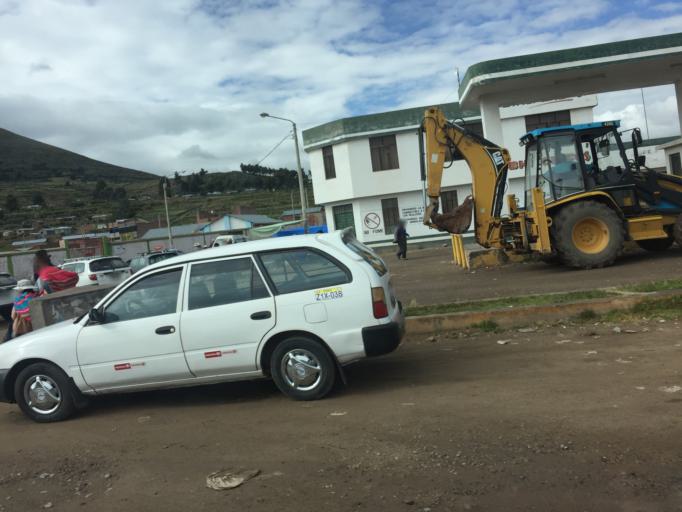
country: PE
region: Puno
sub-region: Provincia de Chucuito
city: Juli
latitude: -16.2196
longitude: -69.4821
